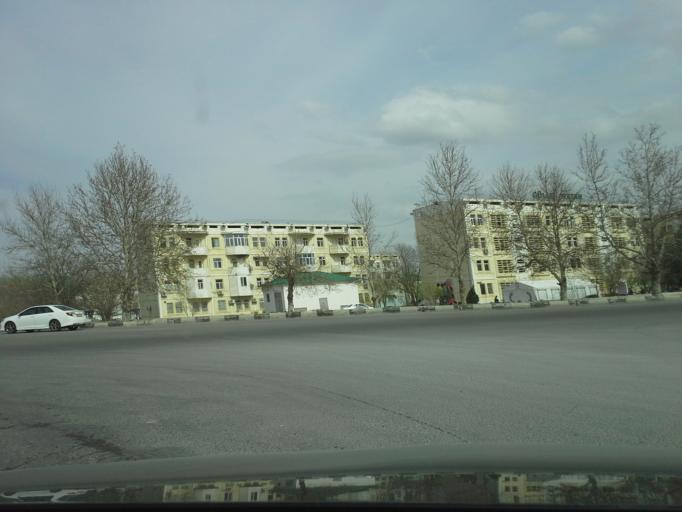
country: TM
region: Ahal
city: Abadan
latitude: 38.0348
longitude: 58.1888
